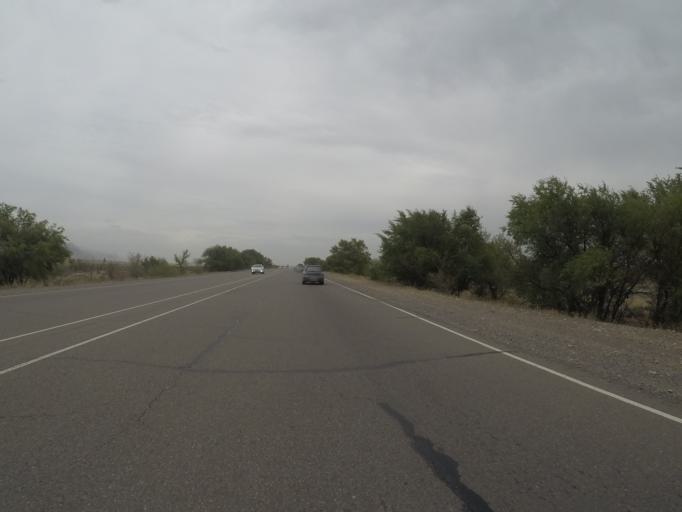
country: KG
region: Chuy
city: Tokmok
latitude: 42.8334
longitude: 75.4411
